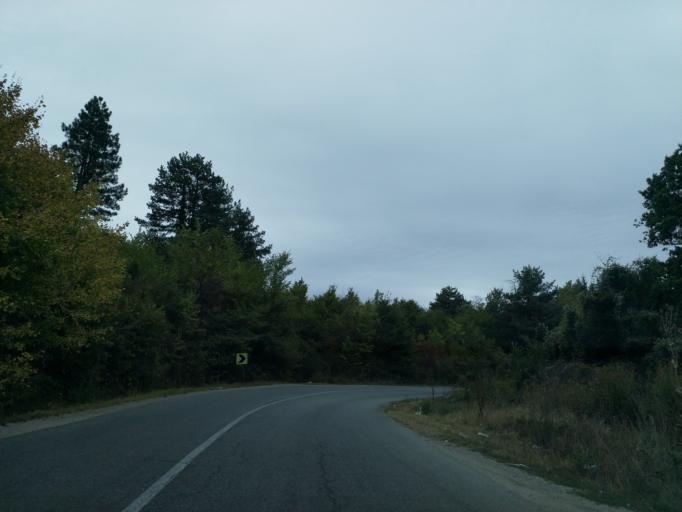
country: RS
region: Central Serbia
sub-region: Pomoravski Okrug
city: Jagodina
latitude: 44.0261
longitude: 21.1979
